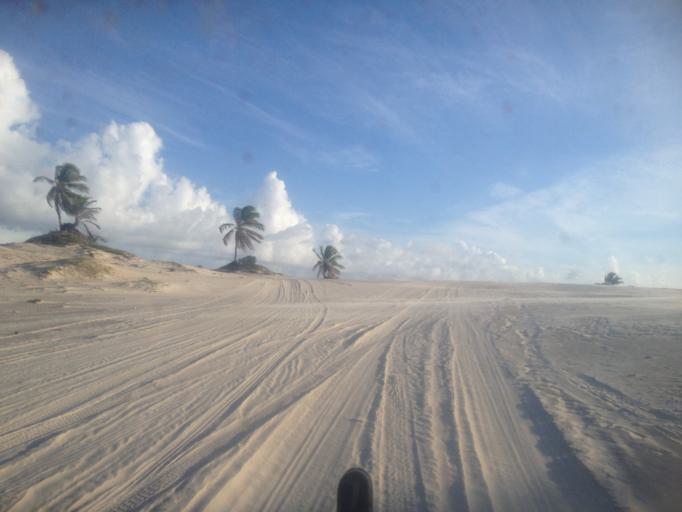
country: BR
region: Sergipe
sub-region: Indiaroba
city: Indiaroba
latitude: -11.4678
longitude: -37.3669
